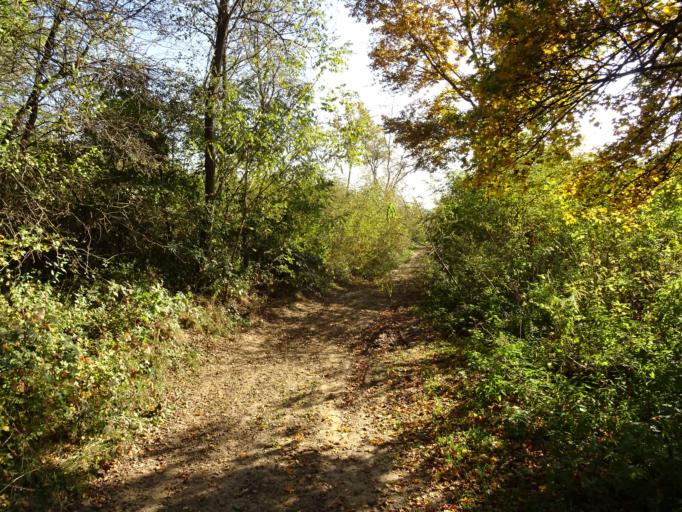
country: HU
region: Nograd
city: Salgotarjan
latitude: 48.1037
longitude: 19.7554
